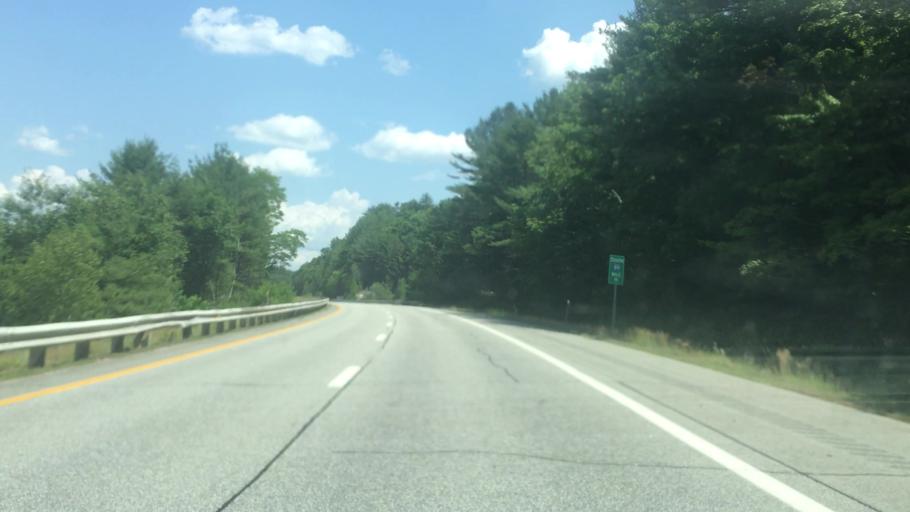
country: US
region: New Hampshire
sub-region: Merrimack County
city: Henniker
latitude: 43.2784
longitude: -71.8245
